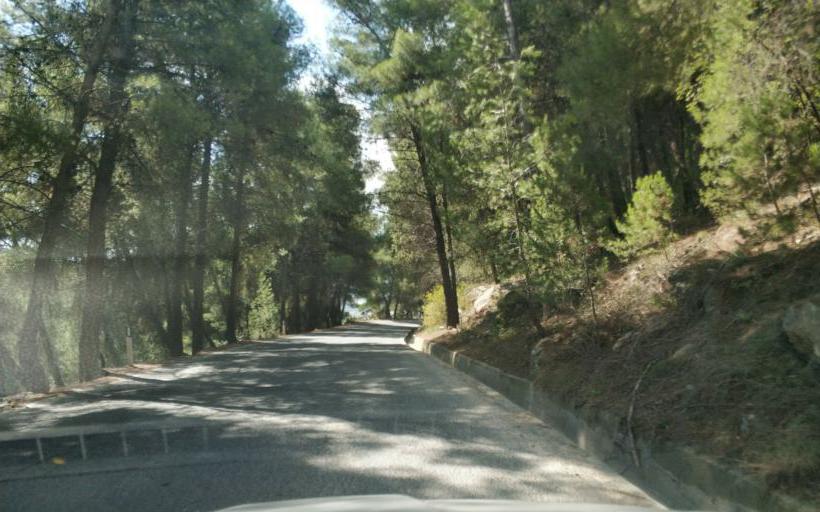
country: AL
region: Durres
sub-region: Rrethi i Krujes
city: Kruje
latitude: 41.4939
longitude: 19.7727
